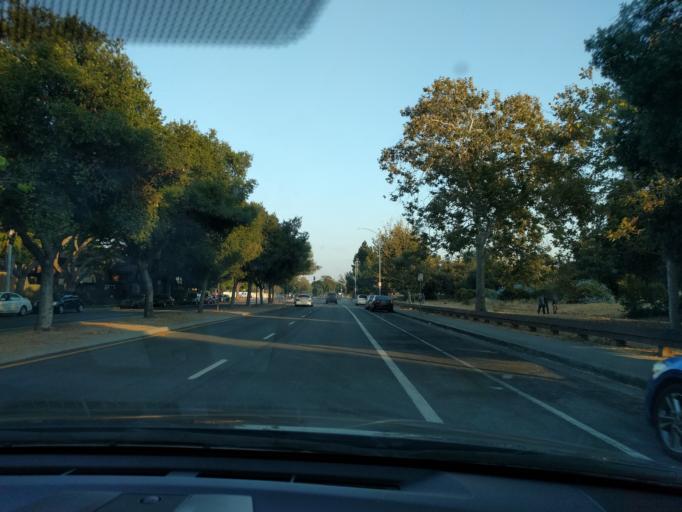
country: US
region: California
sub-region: Santa Clara County
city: Alum Rock
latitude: 37.3751
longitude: -121.8599
